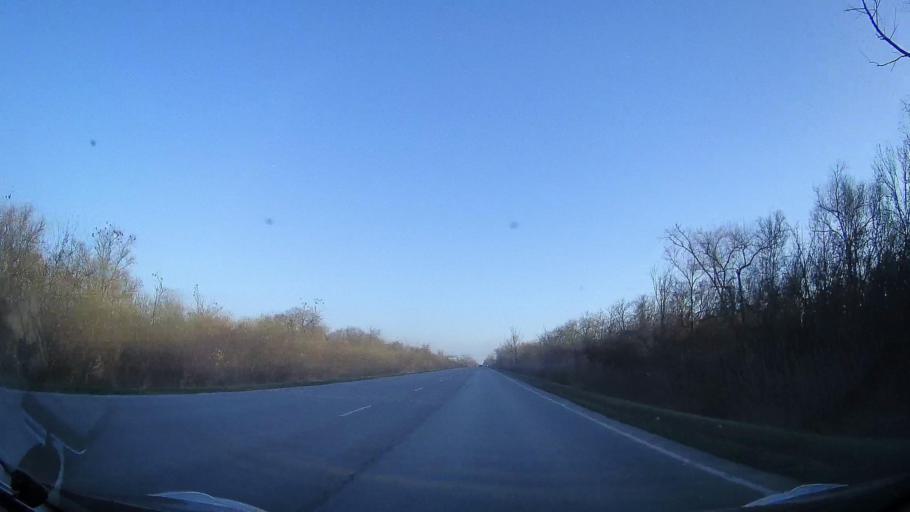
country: RU
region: Rostov
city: Bataysk
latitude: 47.0538
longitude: 39.8308
